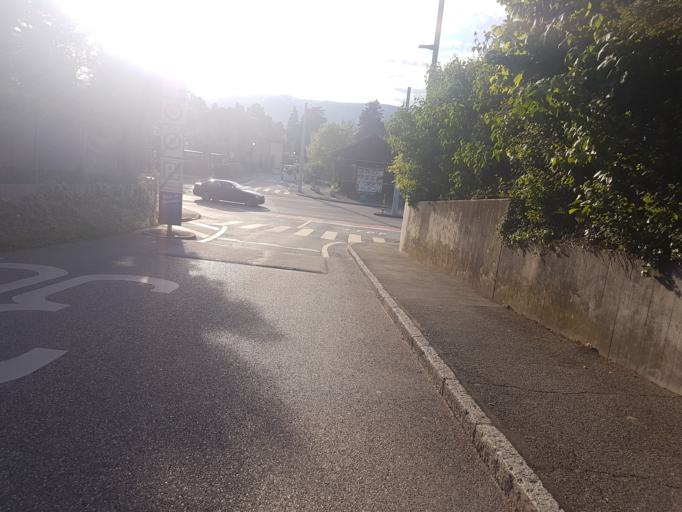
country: CH
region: Geneva
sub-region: Geneva
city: Vernier
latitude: 46.2121
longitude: 6.0791
